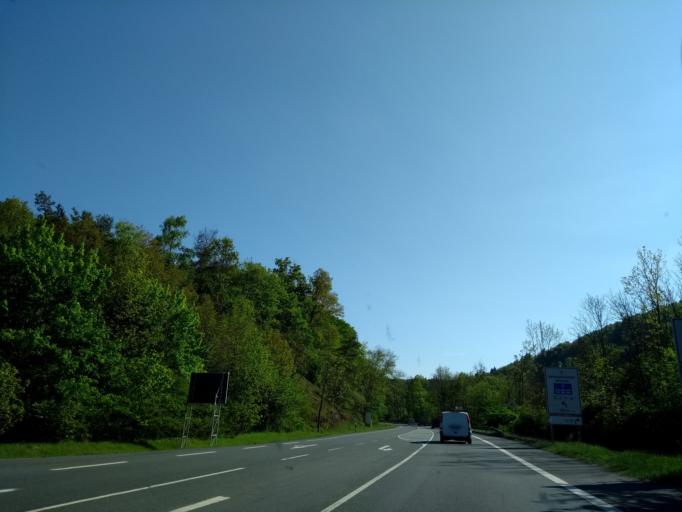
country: DE
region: Hesse
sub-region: Regierungsbezirk Kassel
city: Vohl
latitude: 51.1814
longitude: 8.8877
